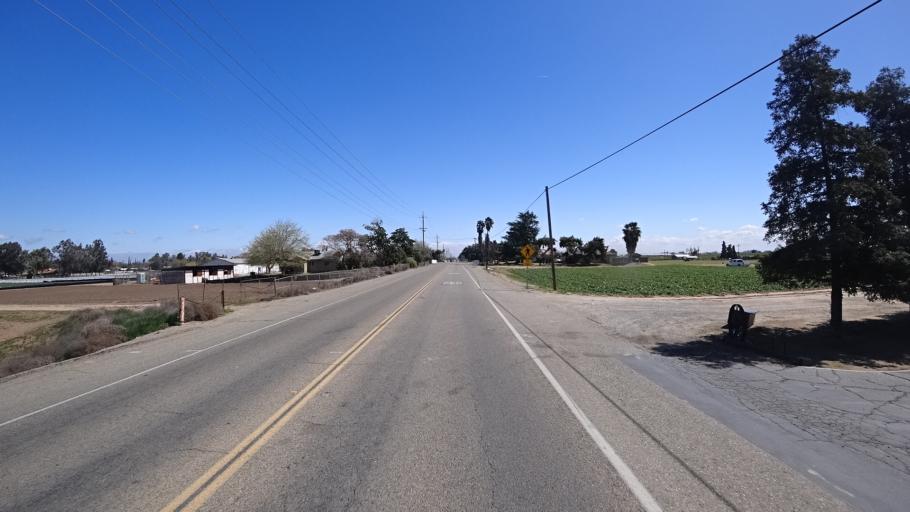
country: US
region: California
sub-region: Fresno County
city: West Park
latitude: 36.7065
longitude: -119.8558
